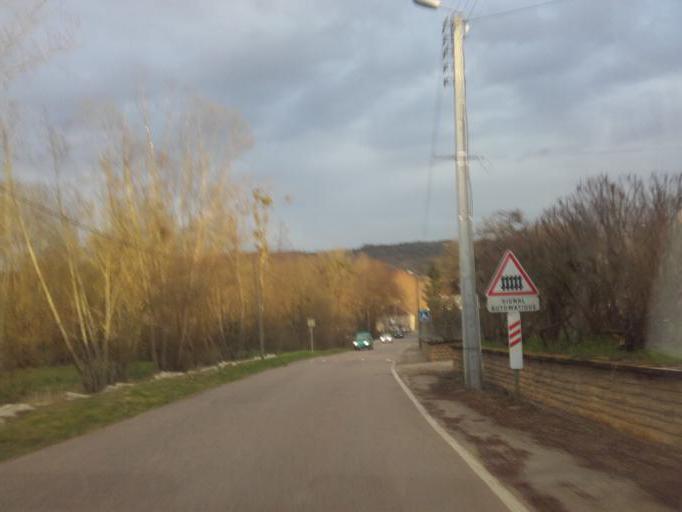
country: FR
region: Bourgogne
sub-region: Departement de Saone-et-Loire
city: Saint-Leger-sur-Dheune
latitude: 46.8941
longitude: 4.6746
